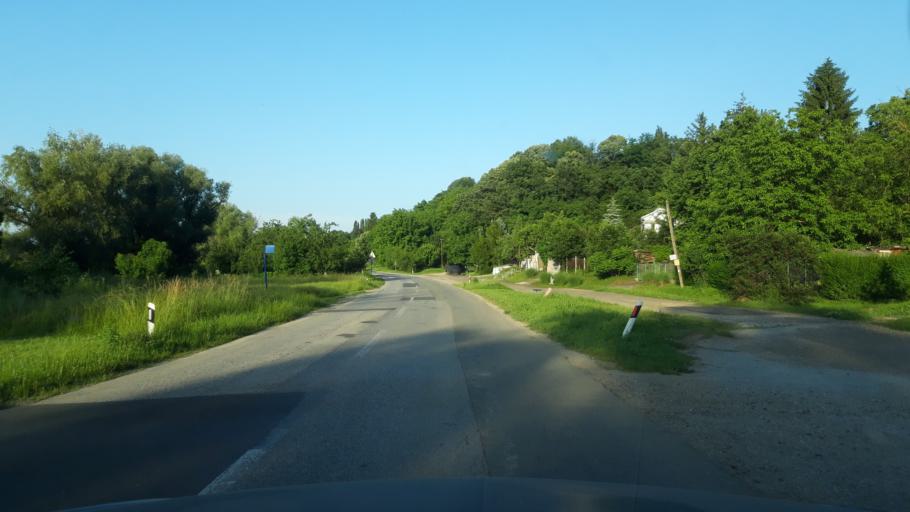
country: RS
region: Autonomna Pokrajina Vojvodina
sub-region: Juznobacki Okrug
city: Beocin
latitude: 45.2173
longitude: 19.6355
